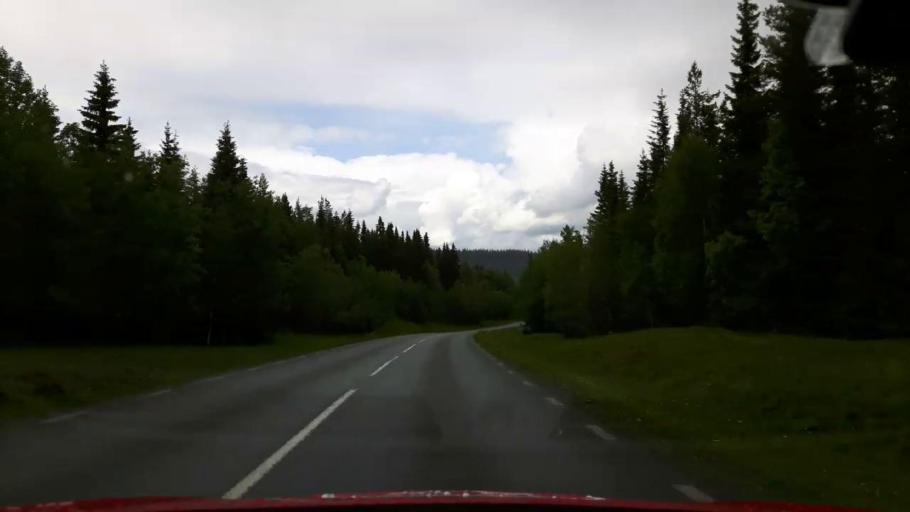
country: SE
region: Jaemtland
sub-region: Krokoms Kommun
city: Krokom
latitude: 63.4721
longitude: 14.1930
